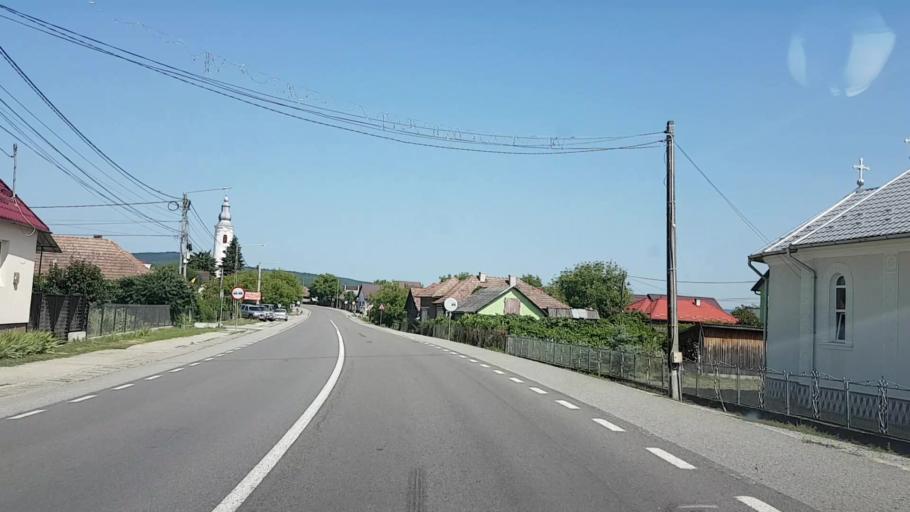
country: RO
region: Bistrita-Nasaud
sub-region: Comuna Uriu
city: Cristestii Ciceului
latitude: 47.1935
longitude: 24.0871
